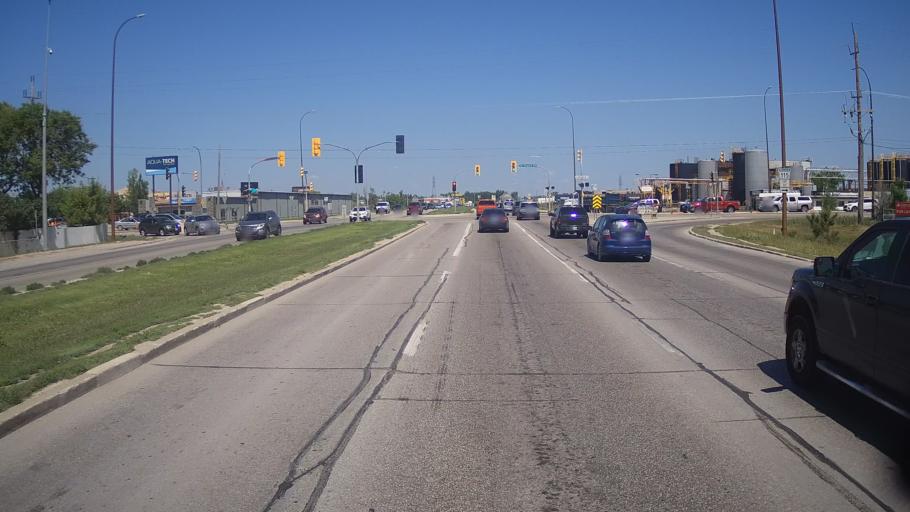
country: CA
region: Manitoba
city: Winnipeg
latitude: 49.8852
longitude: -97.0721
